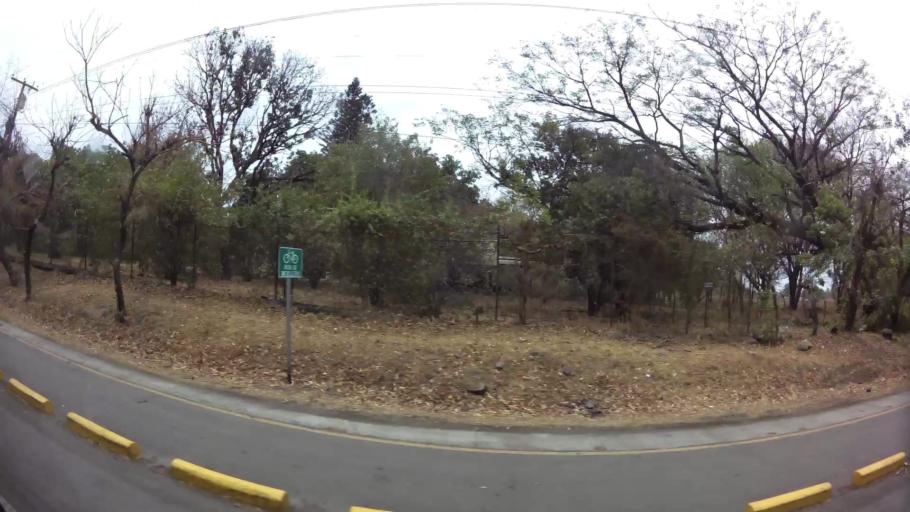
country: NI
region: Leon
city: Leon
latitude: 12.4318
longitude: -86.8643
